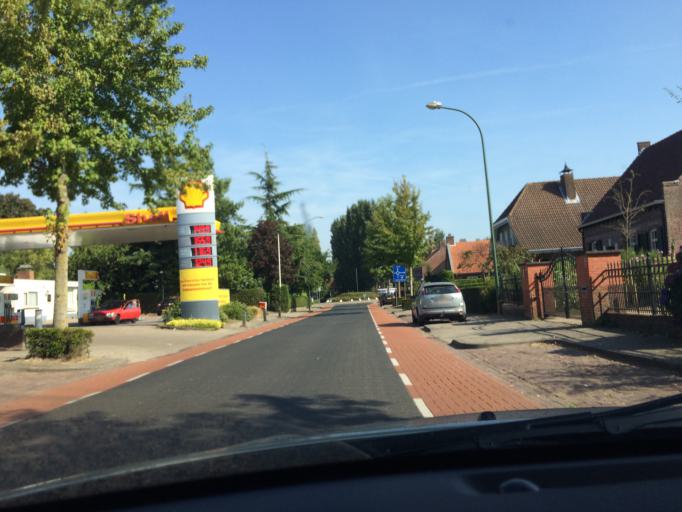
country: NL
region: North Brabant
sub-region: Gemeente Baarle-Nassau
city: Baarle-Nassau
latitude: 51.4459
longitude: 4.9349
